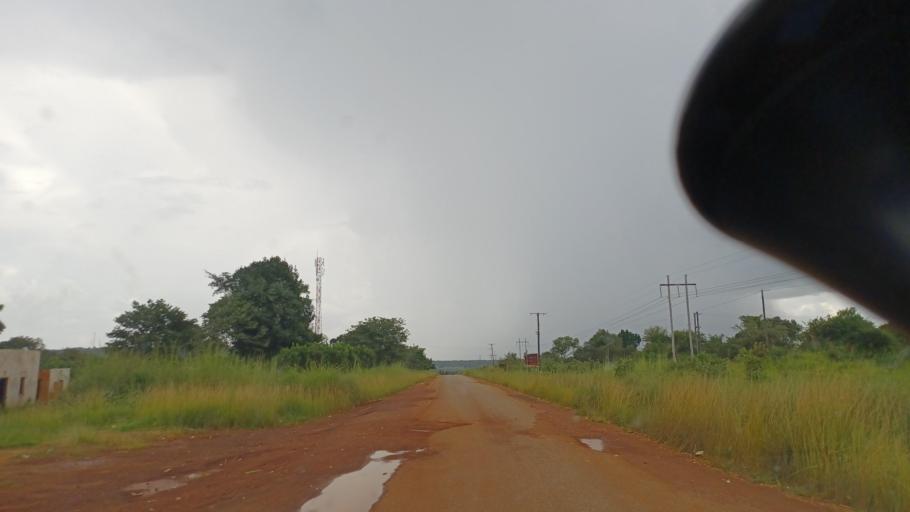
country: ZM
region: North-Western
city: Kasempa
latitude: -13.0547
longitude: 25.9868
